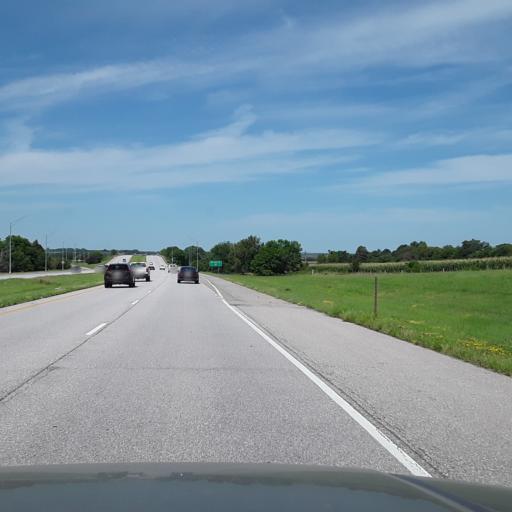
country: US
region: Nebraska
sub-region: Lancaster County
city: Lincoln
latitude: 40.8795
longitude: -96.7510
